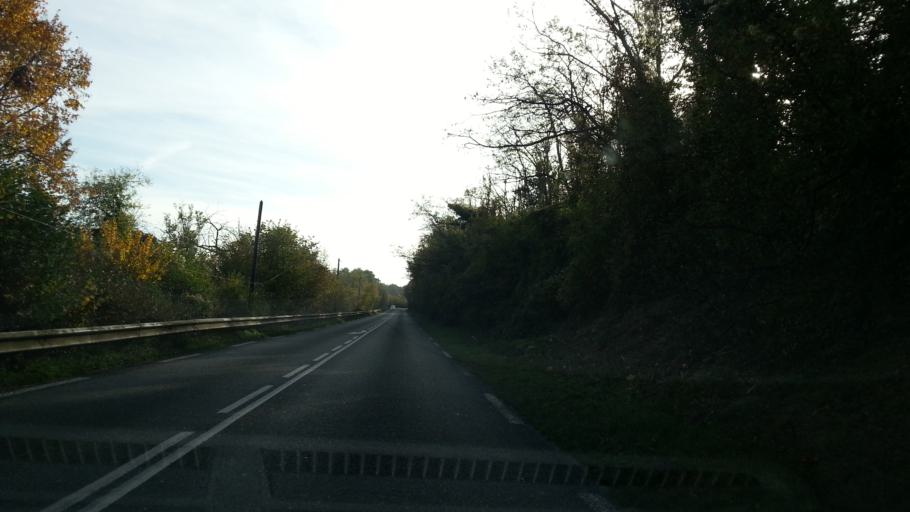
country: FR
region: Picardie
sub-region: Departement de l'Oise
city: Precy-sur-Oise
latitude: 49.1898
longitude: 2.3641
